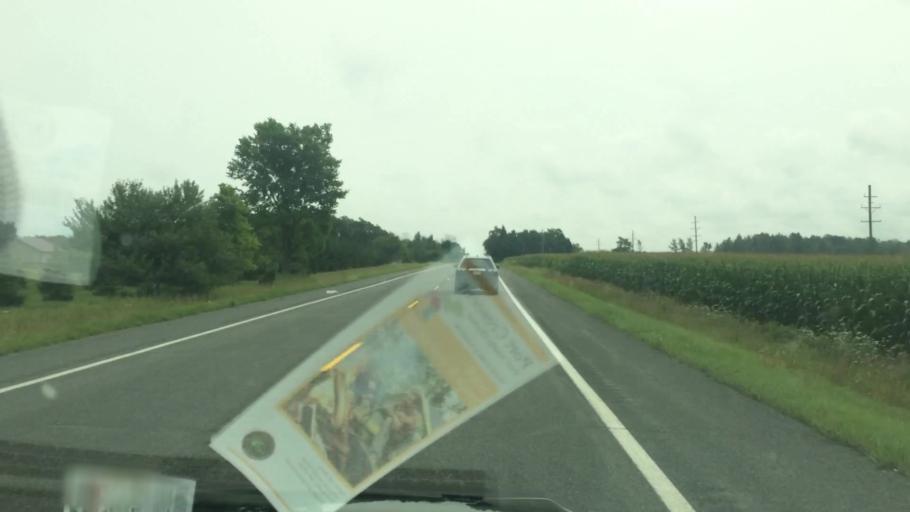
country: US
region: Michigan
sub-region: Huron County
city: Harbor Beach
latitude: 44.0167
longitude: -82.8020
